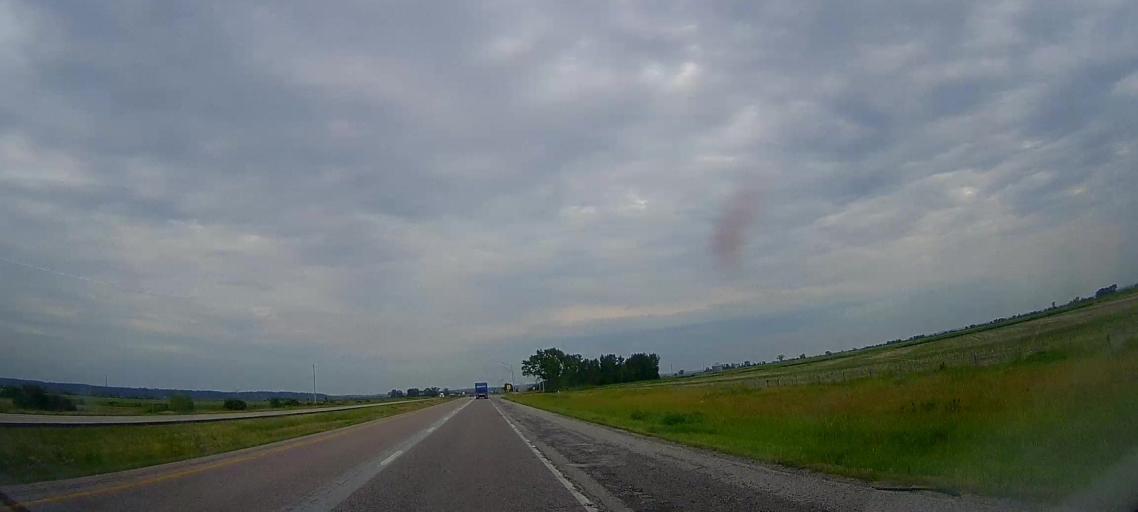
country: US
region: Iowa
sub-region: Harrison County
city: Missouri Valley
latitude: 41.5961
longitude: -95.9575
